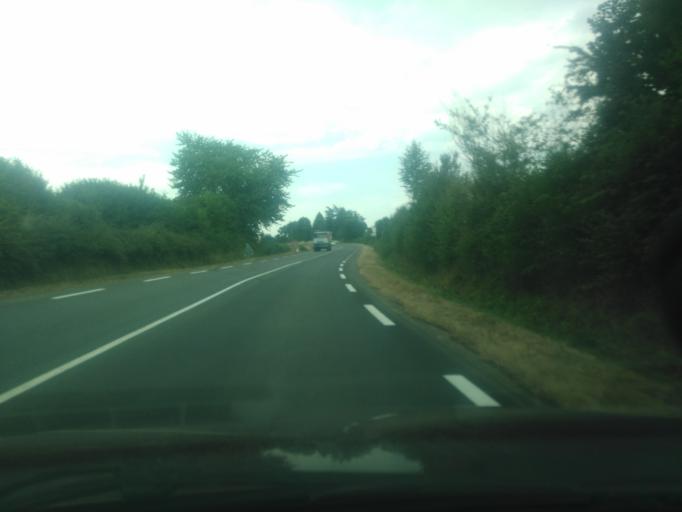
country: FR
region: Poitou-Charentes
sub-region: Departement des Deux-Sevres
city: Secondigny
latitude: 46.6166
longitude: -0.4500
